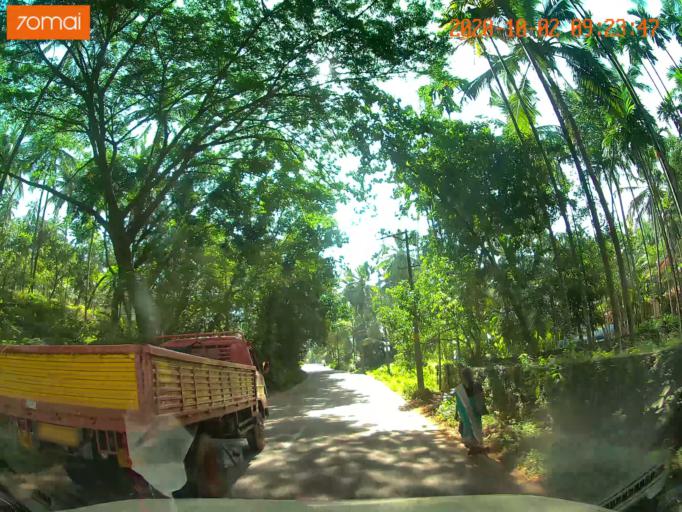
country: IN
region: Kerala
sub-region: Kozhikode
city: Naduvannur
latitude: 11.5835
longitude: 75.7604
